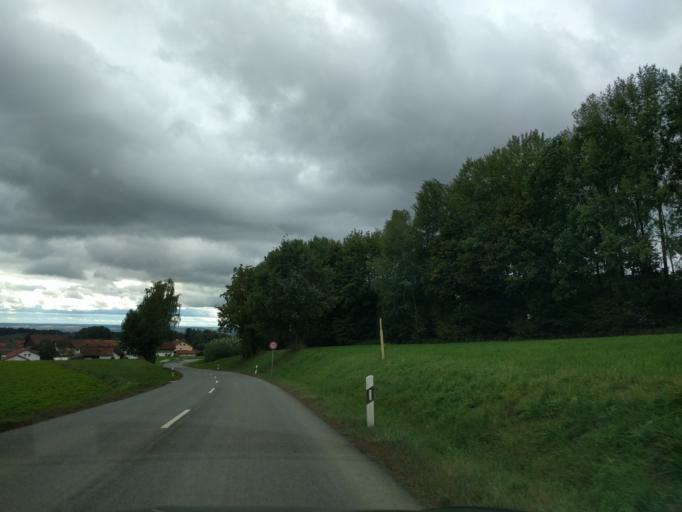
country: DE
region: Bavaria
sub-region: Lower Bavaria
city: Deggendorf
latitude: 48.8360
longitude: 13.0044
